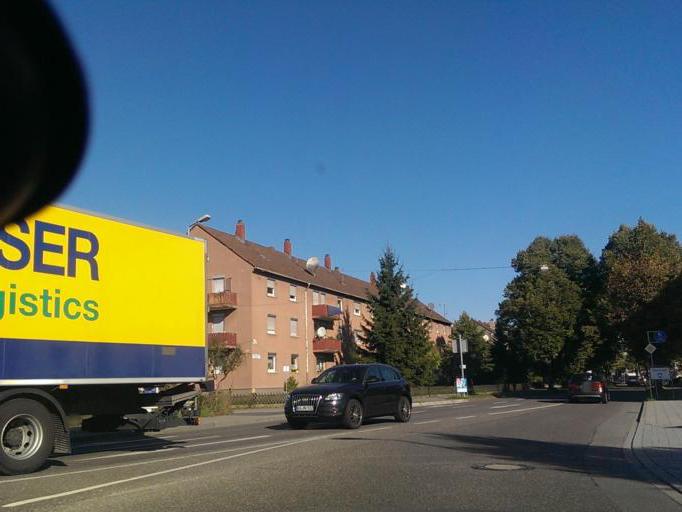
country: DE
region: Baden-Wuerttemberg
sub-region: Karlsruhe Region
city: Karlsruhe
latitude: 49.0037
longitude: 8.4244
